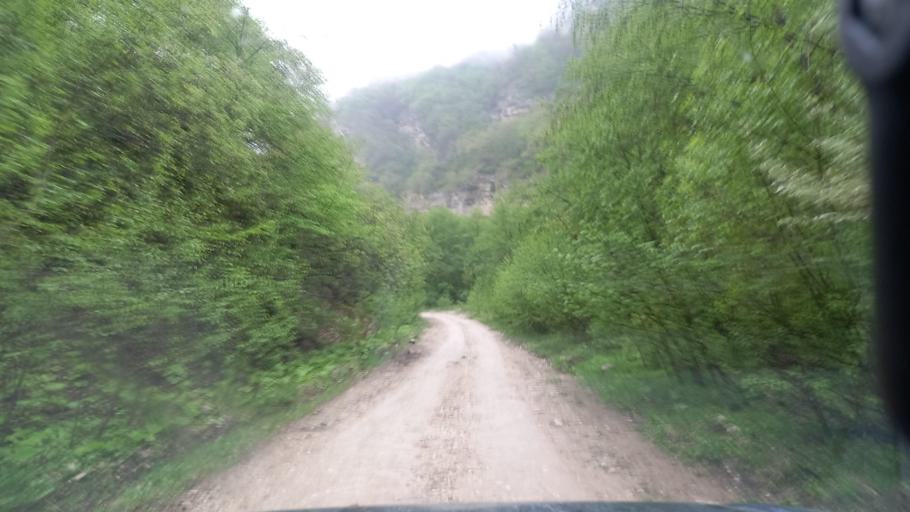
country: RU
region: Kabardino-Balkariya
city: Gundelen
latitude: 43.5828
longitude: 43.1166
